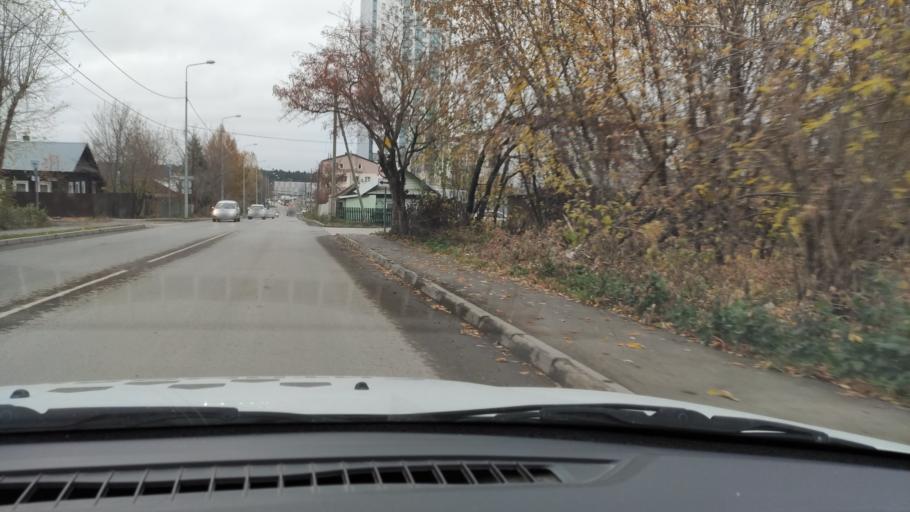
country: RU
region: Perm
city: Kondratovo
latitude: 57.9655
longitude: 56.1551
